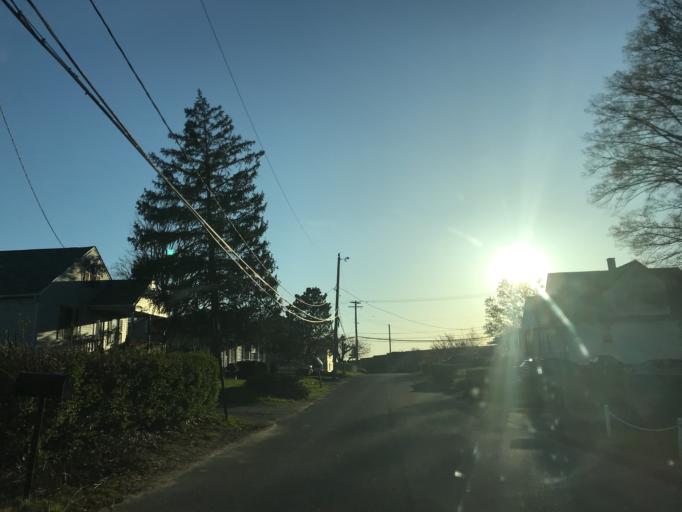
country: US
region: Maryland
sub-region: Baltimore County
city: Rosedale
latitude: 39.3286
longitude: -76.5218
